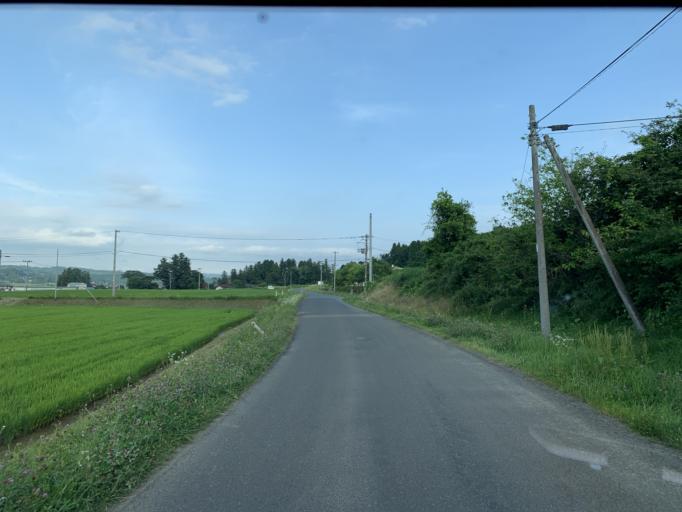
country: JP
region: Iwate
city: Ichinoseki
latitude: 38.8392
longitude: 141.1668
